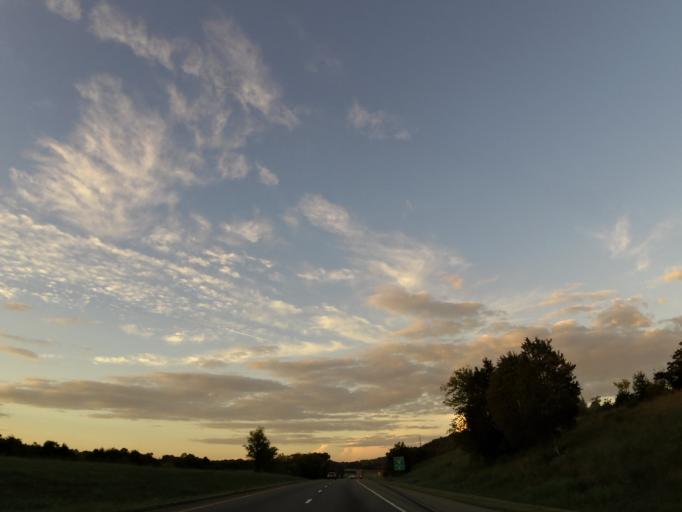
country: US
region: Tennessee
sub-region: McMinn County
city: Athens
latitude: 35.5423
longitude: -84.5719
